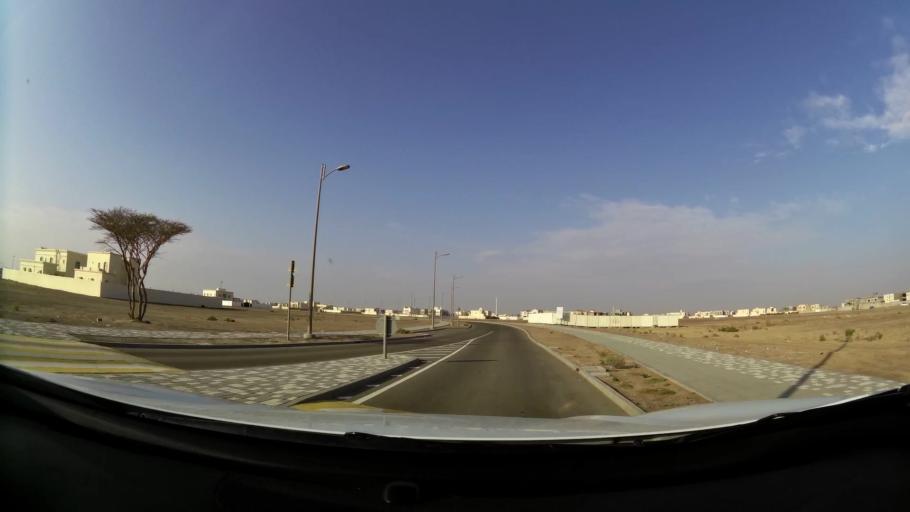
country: AE
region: Abu Dhabi
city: Al Ain
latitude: 24.0992
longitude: 55.8469
